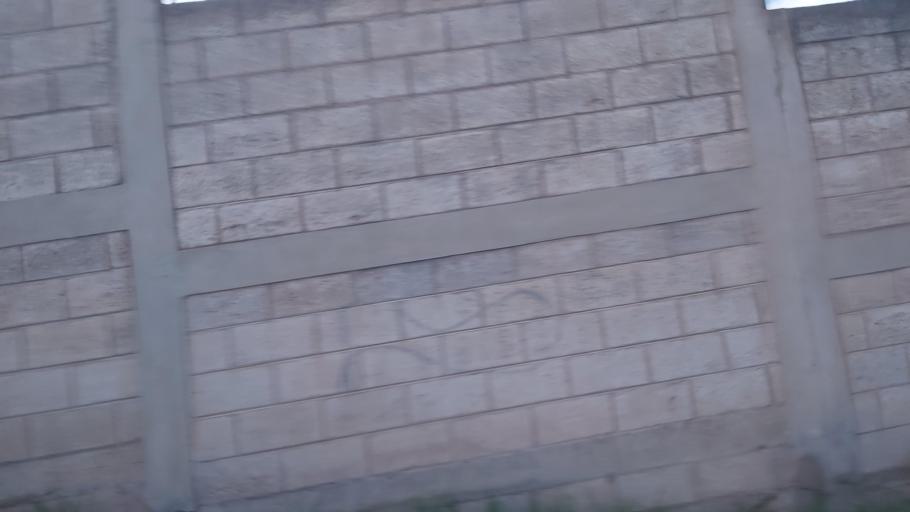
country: GT
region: Quetzaltenango
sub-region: Municipio de La Esperanza
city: La Esperanza
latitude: 14.8539
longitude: -91.5547
